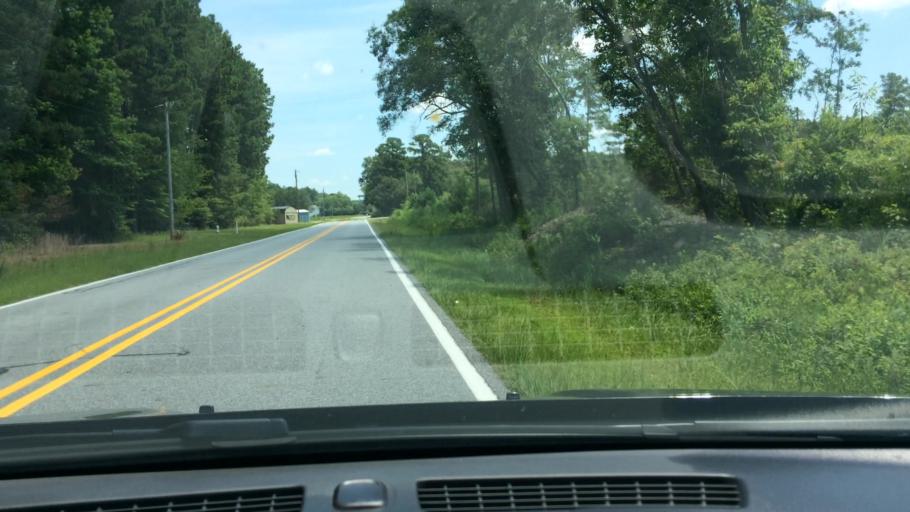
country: US
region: North Carolina
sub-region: Pitt County
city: Windsor
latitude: 35.4967
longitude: -77.3446
